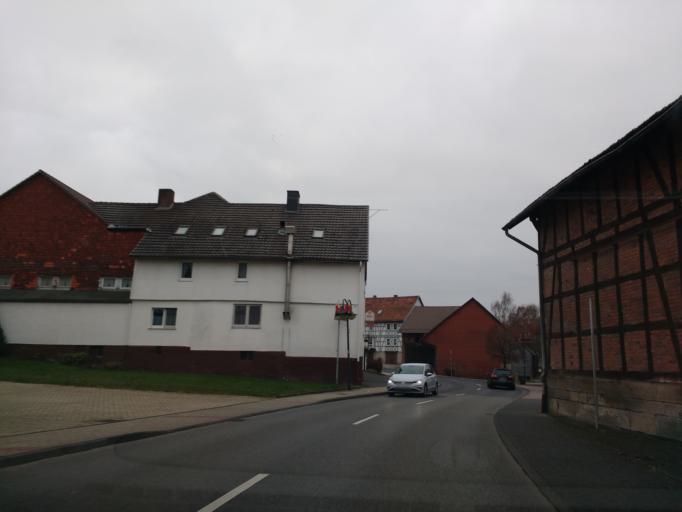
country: DE
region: Hesse
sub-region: Regierungsbezirk Kassel
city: Baunatal
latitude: 51.2290
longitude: 9.4178
